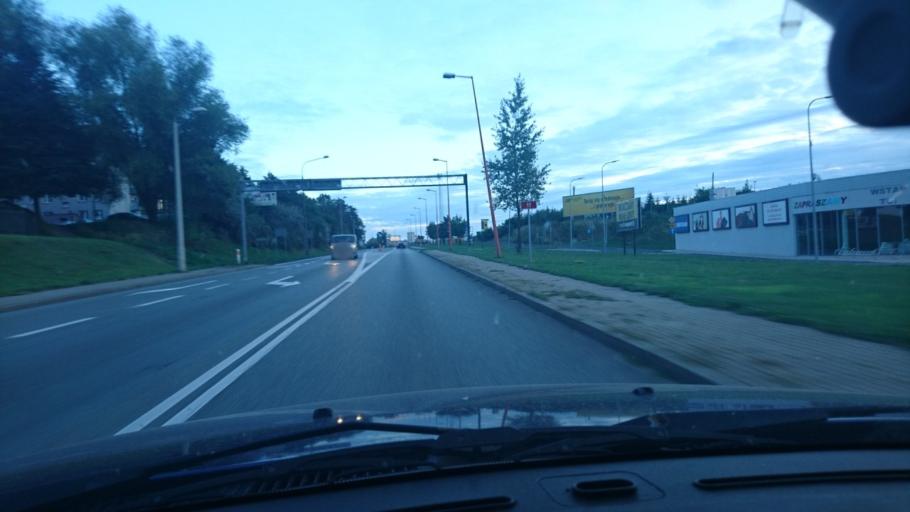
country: PL
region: Silesian Voivodeship
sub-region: Powiat tarnogorski
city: Tarnowskie Gory
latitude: 50.4531
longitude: 18.8382
